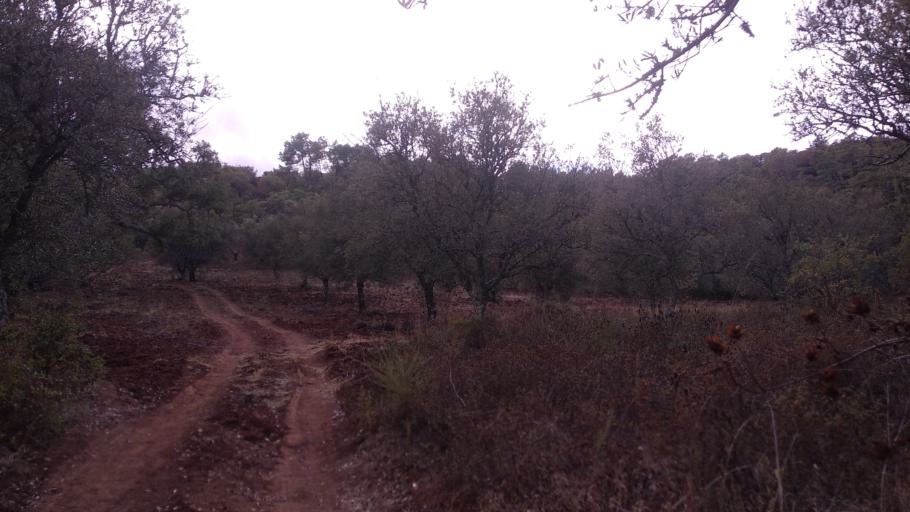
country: PT
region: Faro
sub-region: Sao Bras de Alportel
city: Sao Bras de Alportel
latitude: 37.1617
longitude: -7.9074
